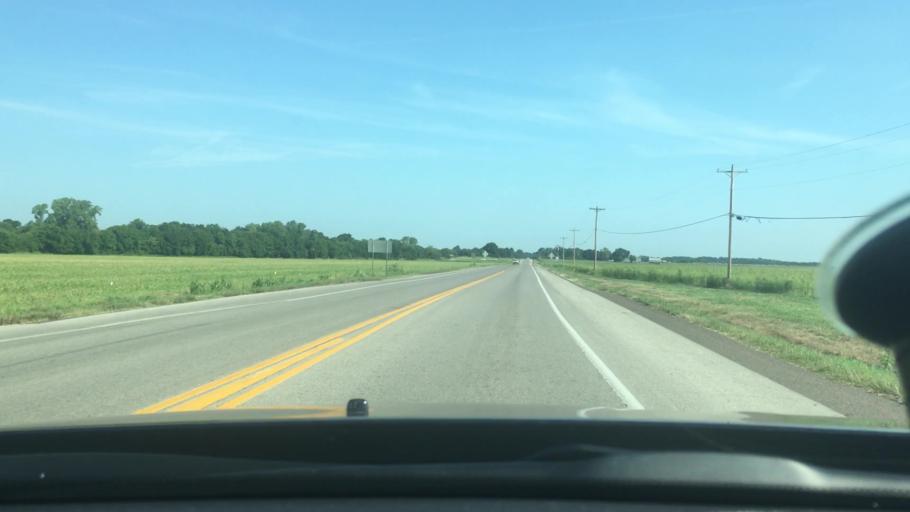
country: US
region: Oklahoma
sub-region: Garvin County
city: Wynnewood
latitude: 34.6529
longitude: -97.2008
